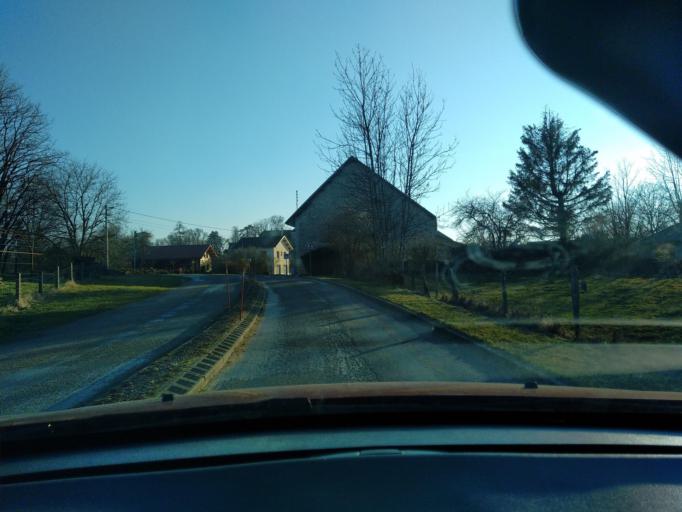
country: FR
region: Franche-Comte
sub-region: Departement du Jura
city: Perrigny
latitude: 46.6356
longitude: 5.6428
